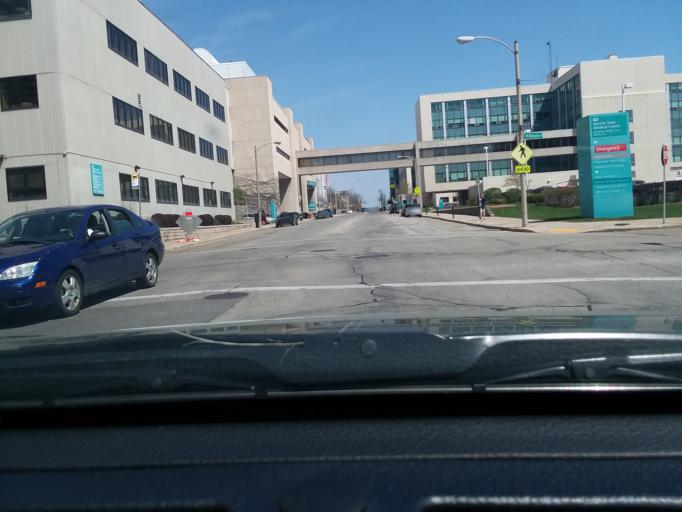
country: US
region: Wisconsin
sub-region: Milwaukee County
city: Milwaukee
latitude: 43.0415
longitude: -87.9271
